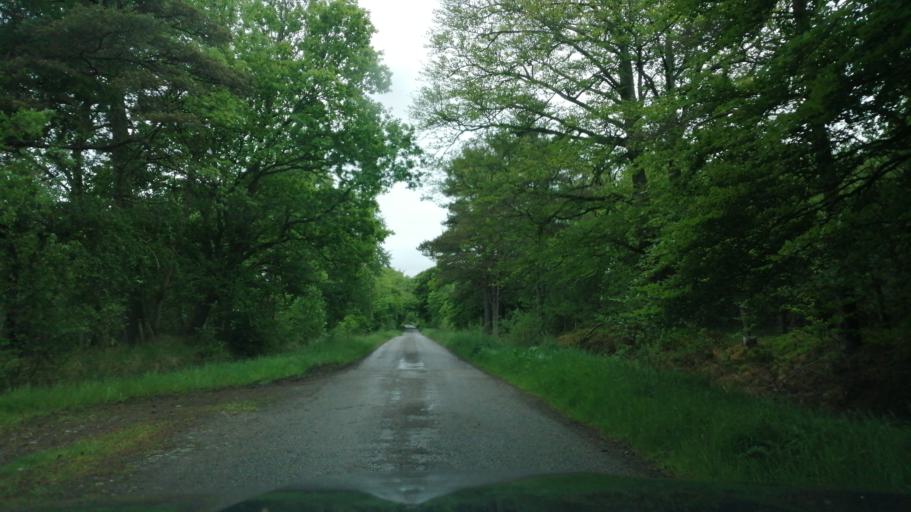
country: GB
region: Scotland
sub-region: Moray
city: Cullen
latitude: 57.5726
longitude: -2.8300
